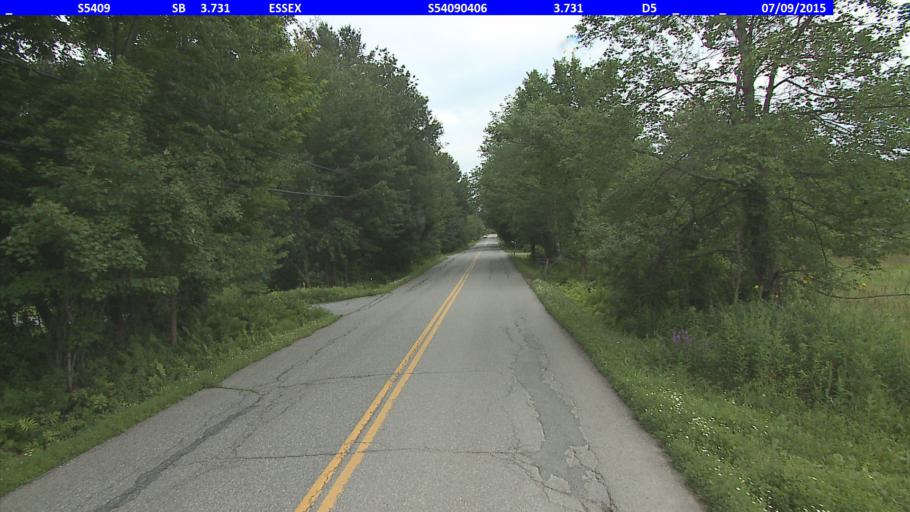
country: US
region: Vermont
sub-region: Chittenden County
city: Essex Junction
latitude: 44.5611
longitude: -73.0639
